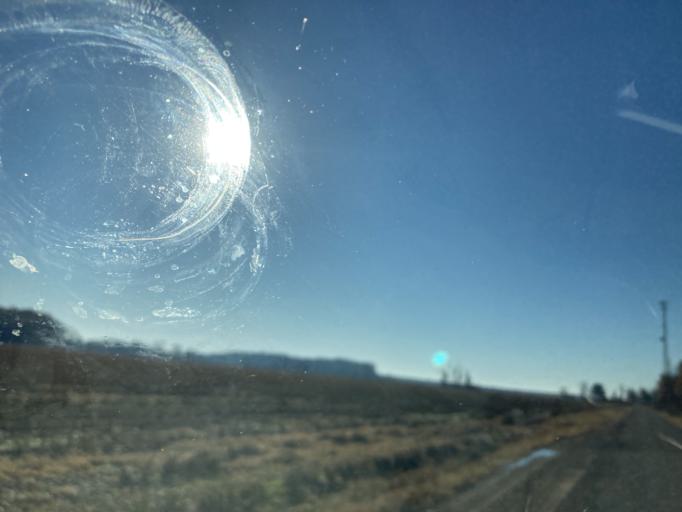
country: US
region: Mississippi
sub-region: Yazoo County
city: Yazoo City
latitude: 32.9211
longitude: -90.5887
